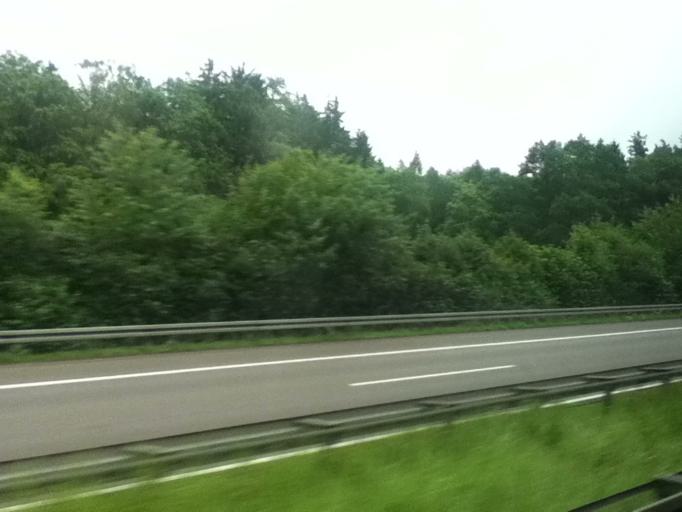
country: DE
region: Hesse
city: Kirtorf
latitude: 50.7172
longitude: 9.0831
